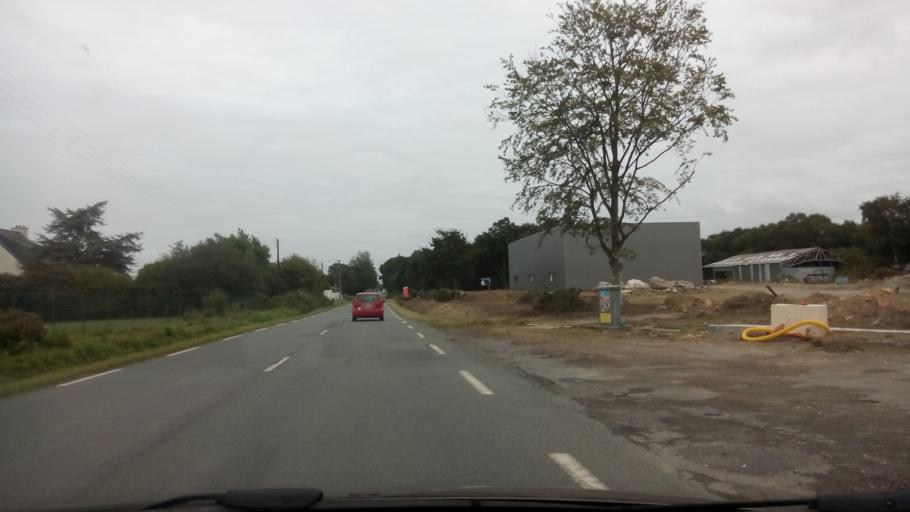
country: FR
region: Brittany
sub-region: Departement des Cotes-d'Armor
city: Ploumilliau
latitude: 48.6982
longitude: -3.5360
